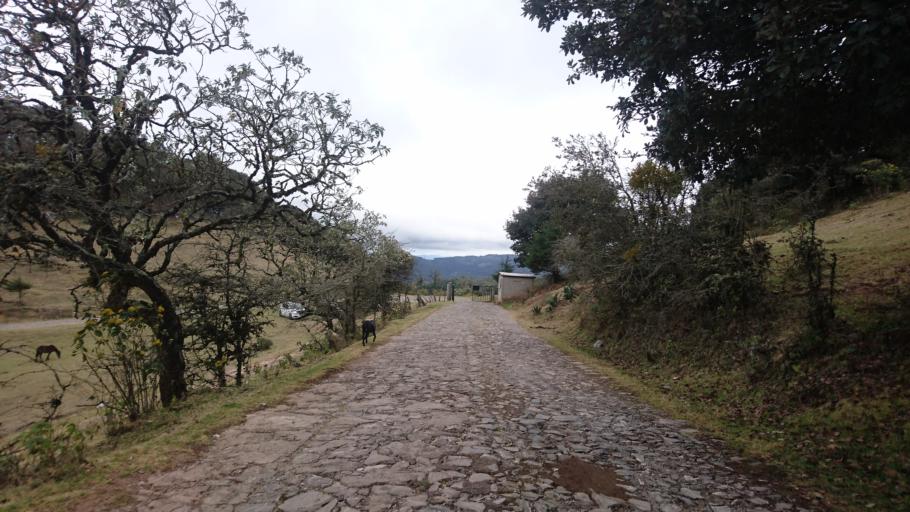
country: MX
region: San Luis Potosi
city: Zaragoza
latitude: 22.0730
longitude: -100.6383
